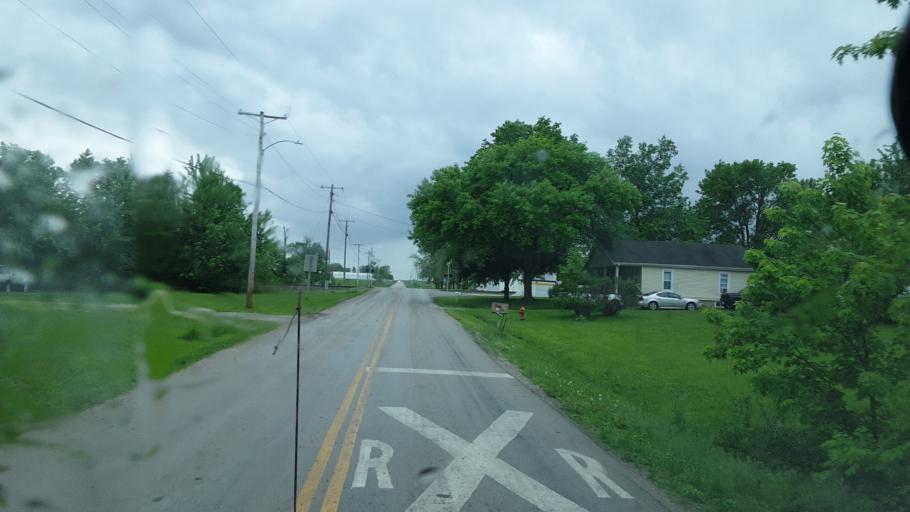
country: US
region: Missouri
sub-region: Monroe County
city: Paris
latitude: 39.4706
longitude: -92.2125
